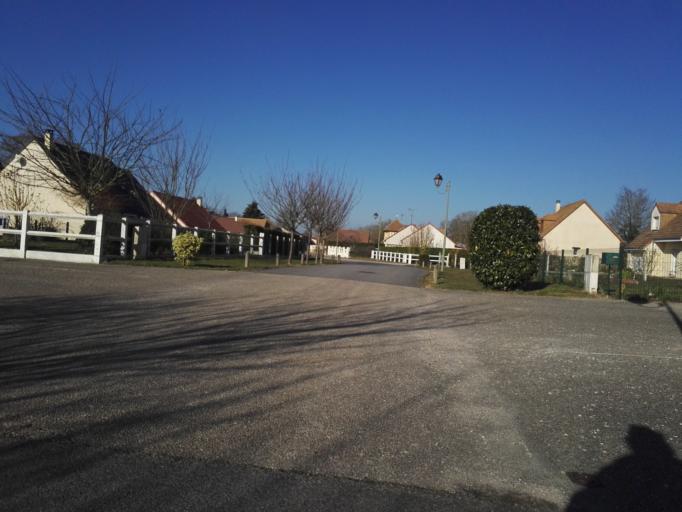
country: FR
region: Haute-Normandie
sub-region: Departement de l'Eure
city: Pacy-sur-Eure
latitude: 49.0063
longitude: 1.4223
